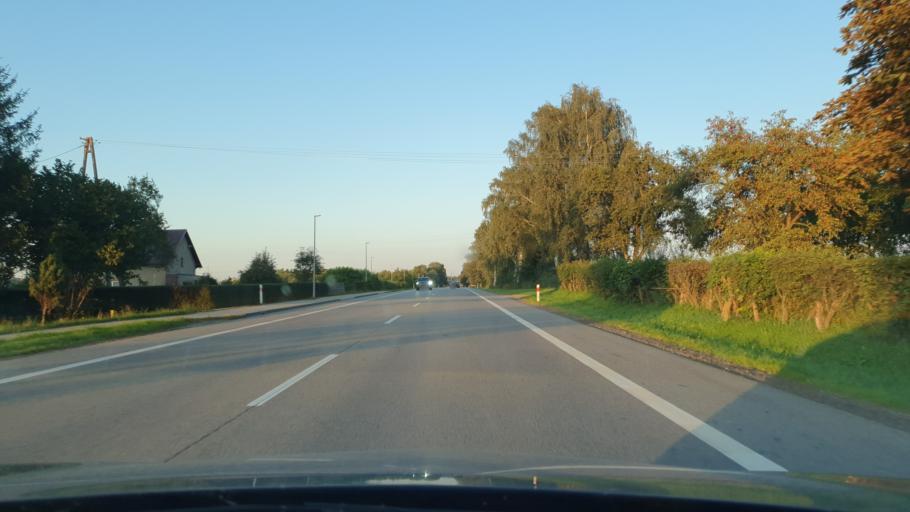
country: PL
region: Pomeranian Voivodeship
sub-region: Powiat slupski
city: Potegowo
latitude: 54.4717
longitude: 17.4796
